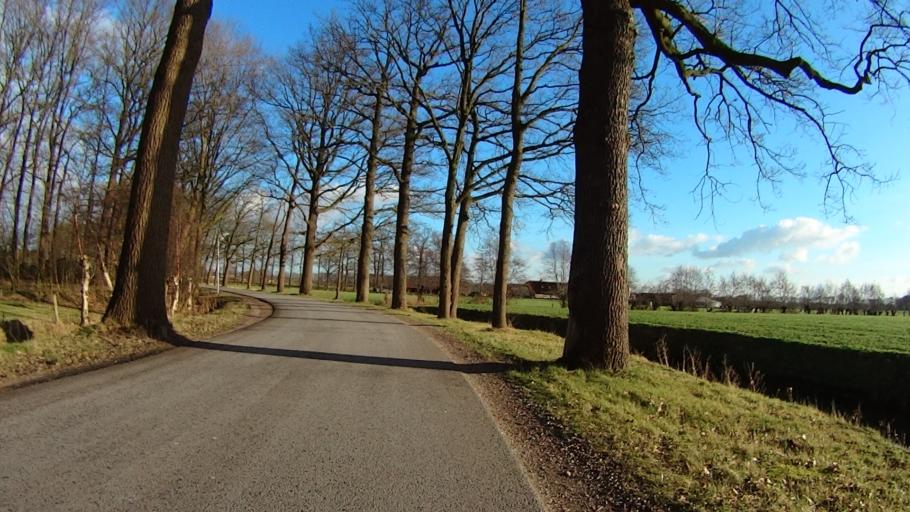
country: NL
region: Utrecht
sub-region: Gemeente Leusden
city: Leusden
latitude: 52.1622
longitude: 5.4478
